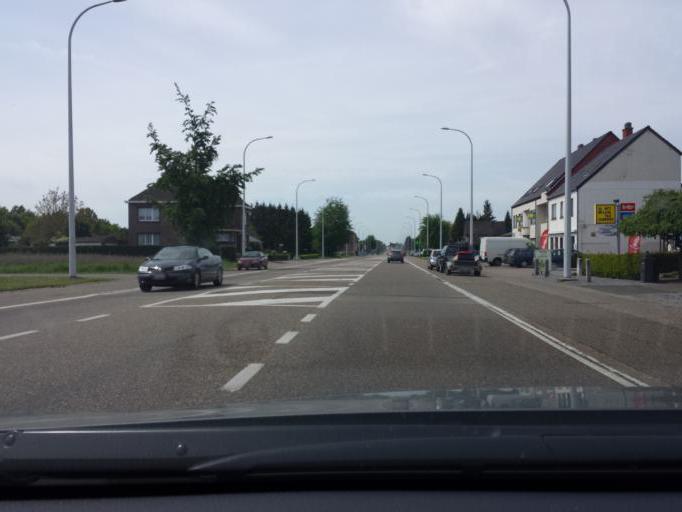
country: BE
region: Flanders
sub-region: Provincie Limburg
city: Lummen
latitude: 50.9478
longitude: 5.2276
